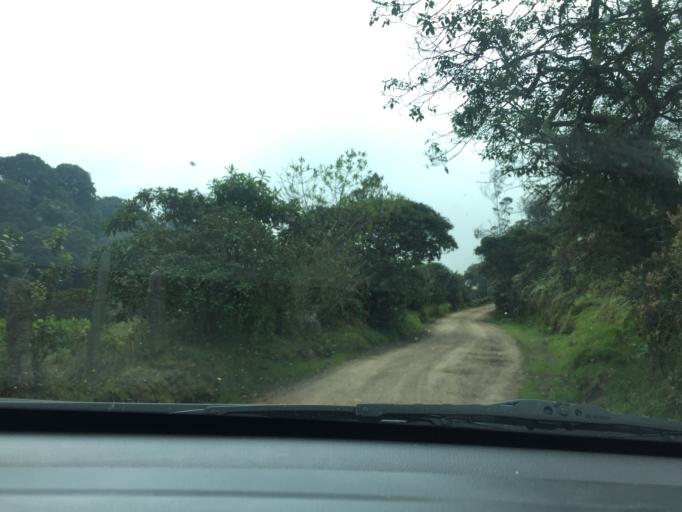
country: CO
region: Cundinamarca
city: Bojaca
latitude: 4.7078
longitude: -74.3498
